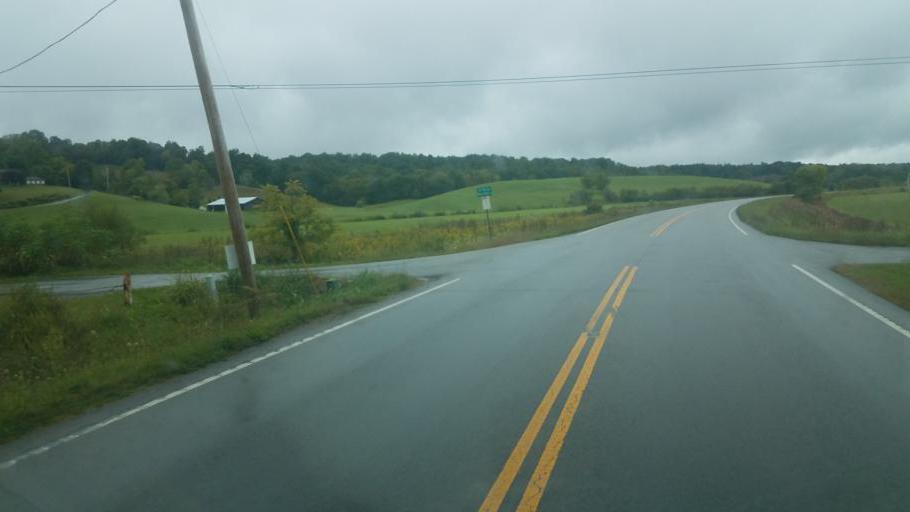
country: US
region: Ohio
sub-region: Jackson County
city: Oak Hill
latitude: 38.8023
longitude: -82.7041
